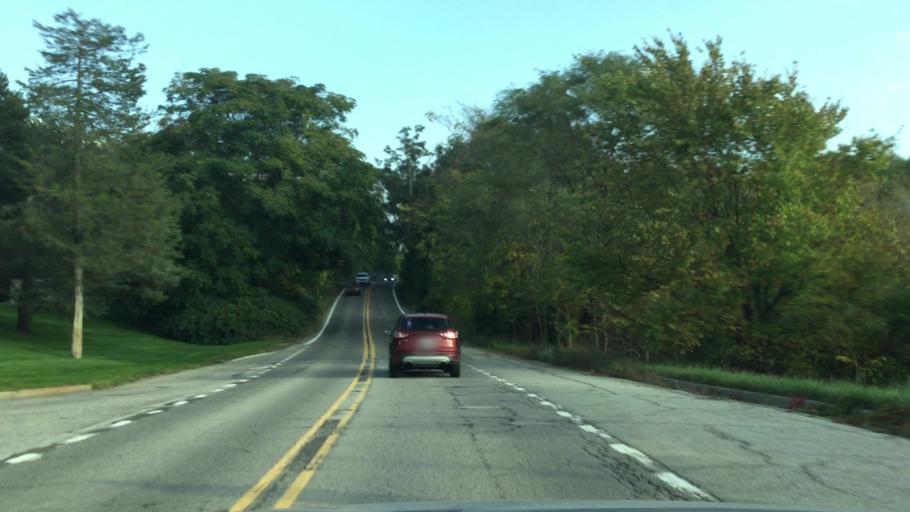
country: US
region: Michigan
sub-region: Oakland County
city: Wolverine Lake
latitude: 42.6226
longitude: -83.4536
